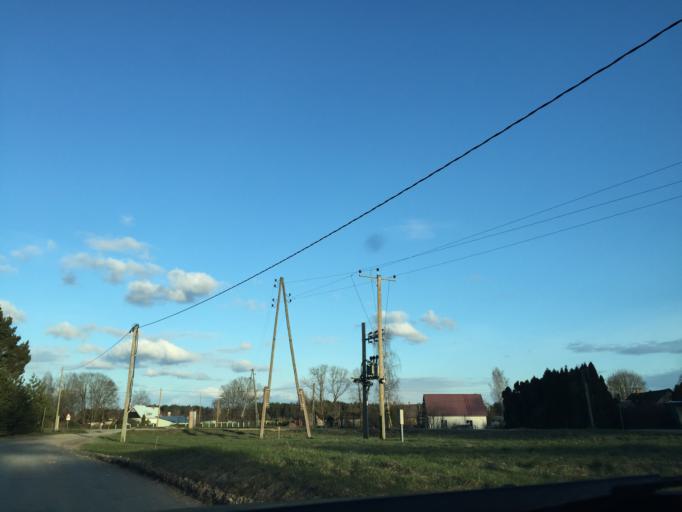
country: LV
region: Kekava
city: Kekava
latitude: 56.8500
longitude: 24.2296
